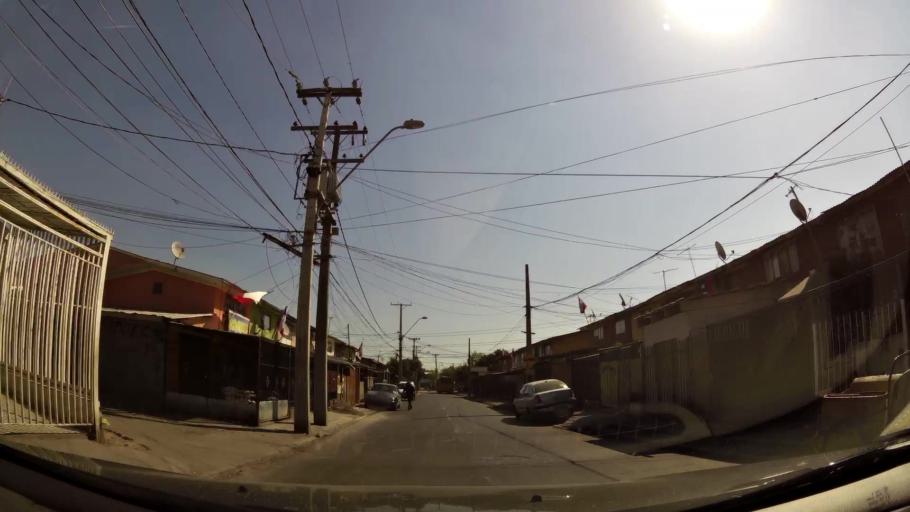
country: CL
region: Santiago Metropolitan
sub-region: Provincia de Santiago
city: La Pintana
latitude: -33.6264
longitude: -70.6218
